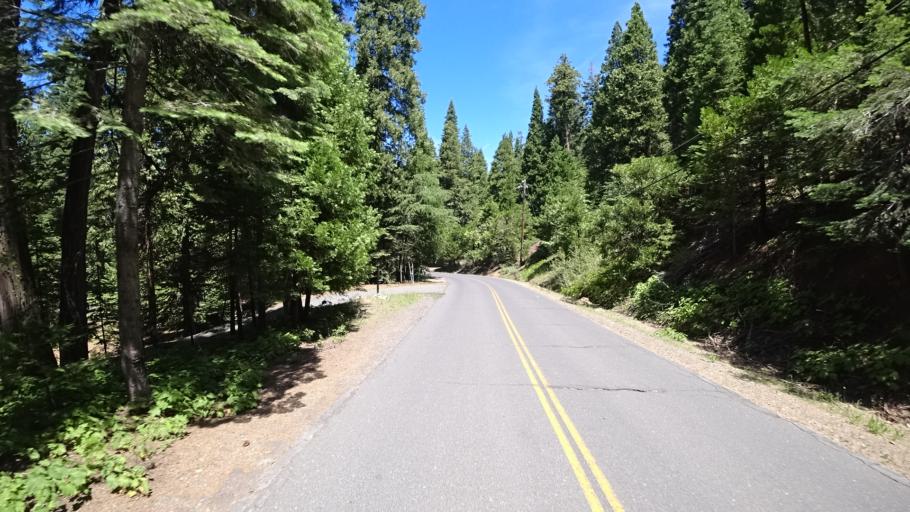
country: US
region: California
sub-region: Calaveras County
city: Arnold
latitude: 38.3113
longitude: -120.2620
